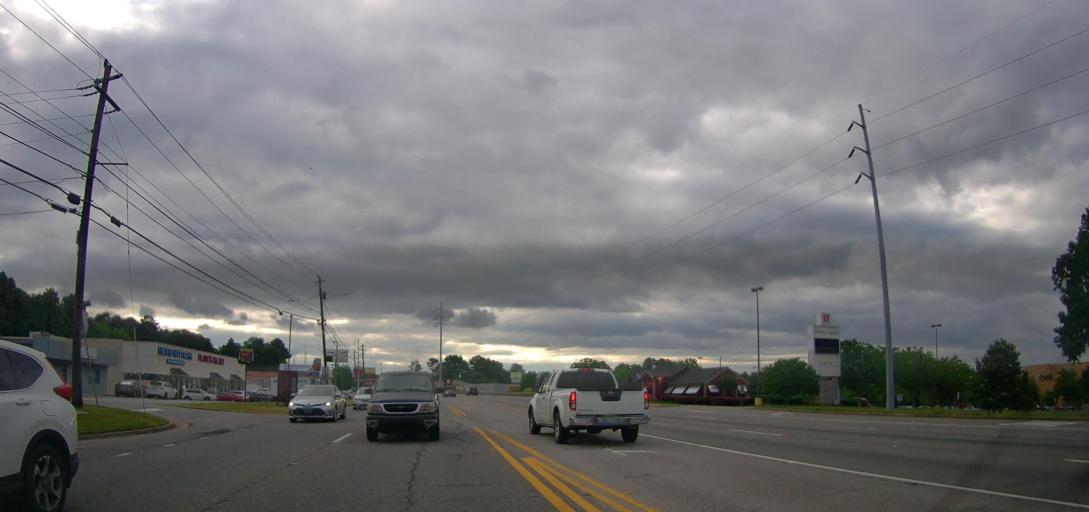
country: US
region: Georgia
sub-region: Oconee County
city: Bogart
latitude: 33.9408
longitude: -83.4664
